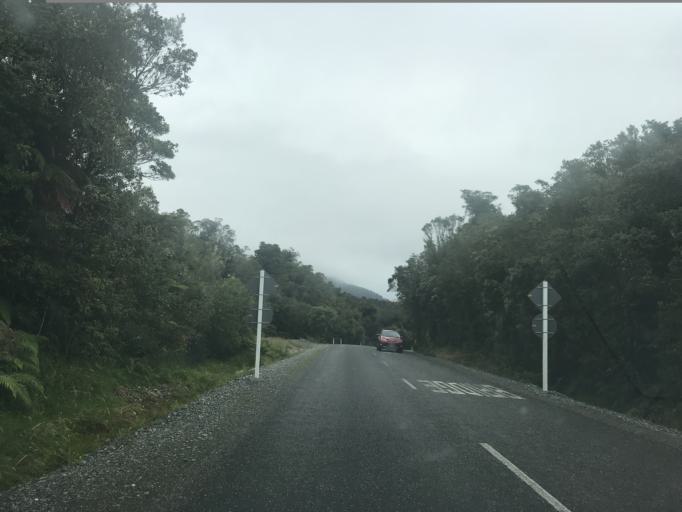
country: NZ
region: West Coast
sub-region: Westland District
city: Hokitika
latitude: -42.9537
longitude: 171.0228
